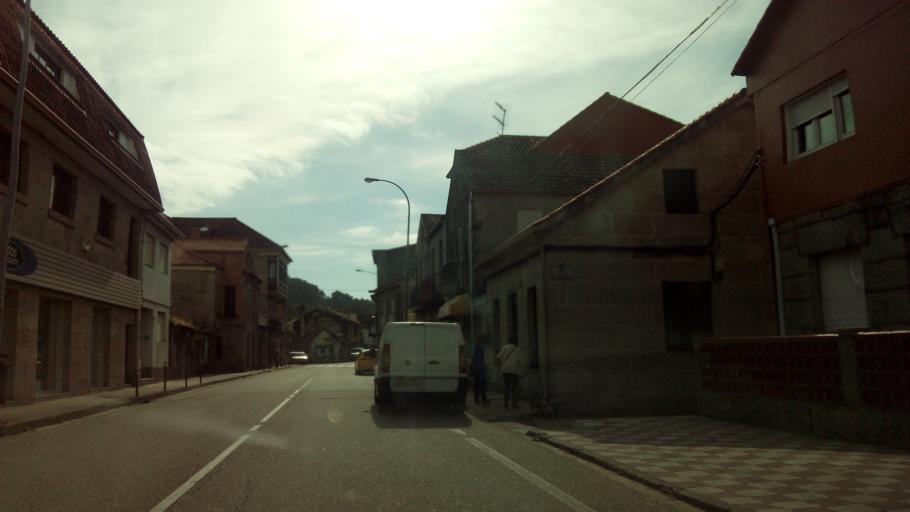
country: ES
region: Galicia
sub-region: Provincia de Pontevedra
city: Baiona
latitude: 42.1100
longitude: -8.8228
